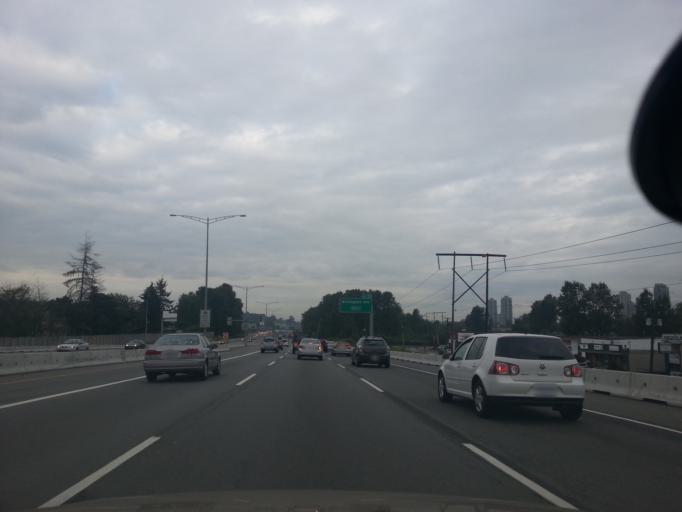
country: CA
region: British Columbia
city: Burnaby
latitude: 49.2579
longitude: -122.9893
